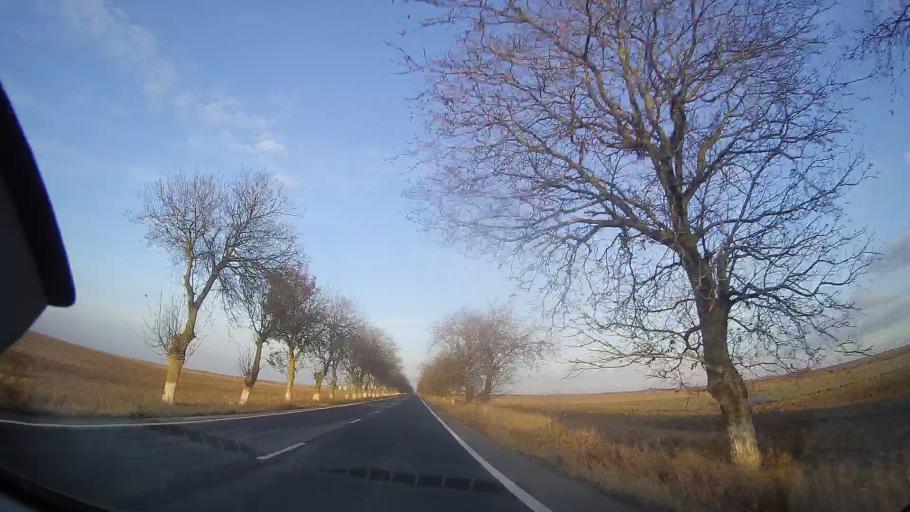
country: RO
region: Constanta
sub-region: Comuna Comana
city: Comana
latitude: 43.8838
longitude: 28.2974
